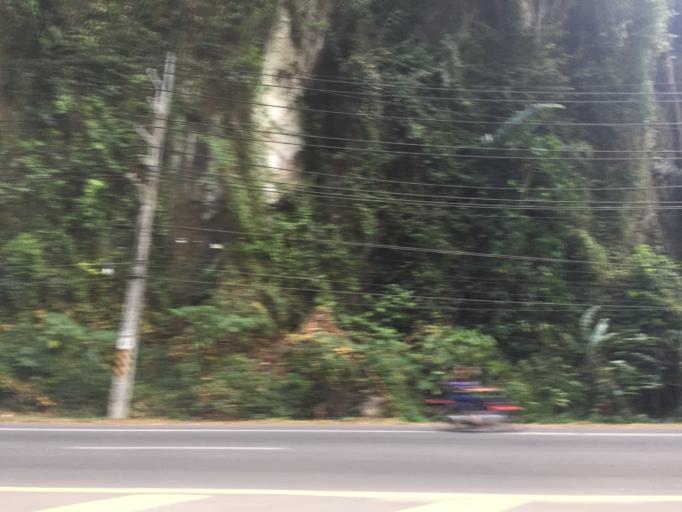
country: TH
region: Phangnga
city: Ban Ao Nang
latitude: 8.0752
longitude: 98.8422
